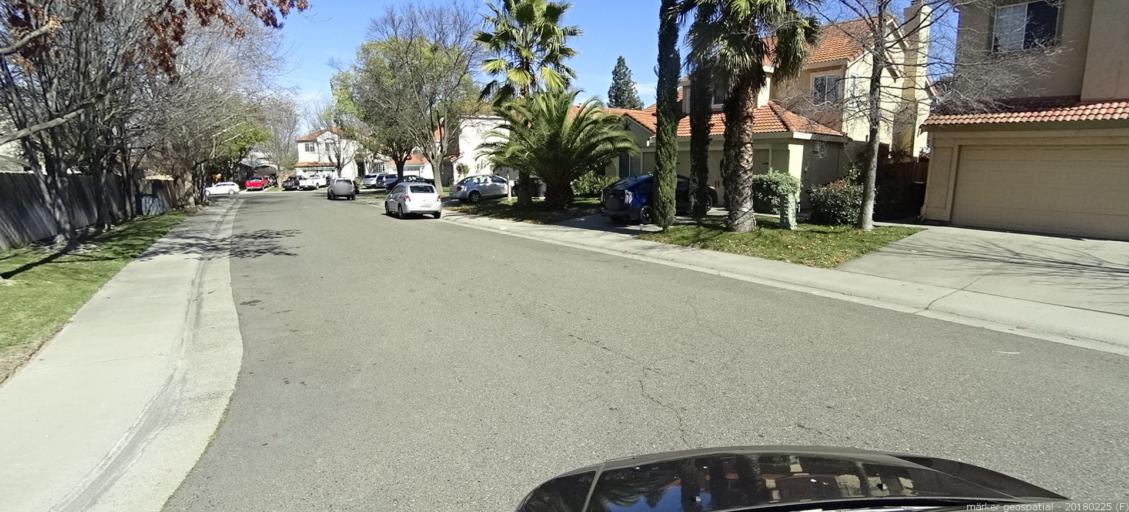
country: US
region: California
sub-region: Sacramento County
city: Antelope
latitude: 38.7194
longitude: -121.3600
